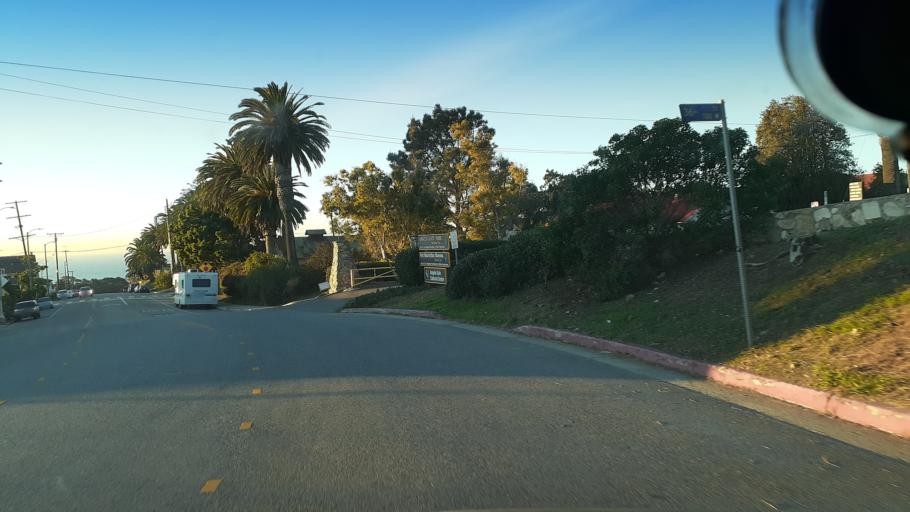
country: US
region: California
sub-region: Los Angeles County
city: San Pedro
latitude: 33.7117
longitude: -118.2929
